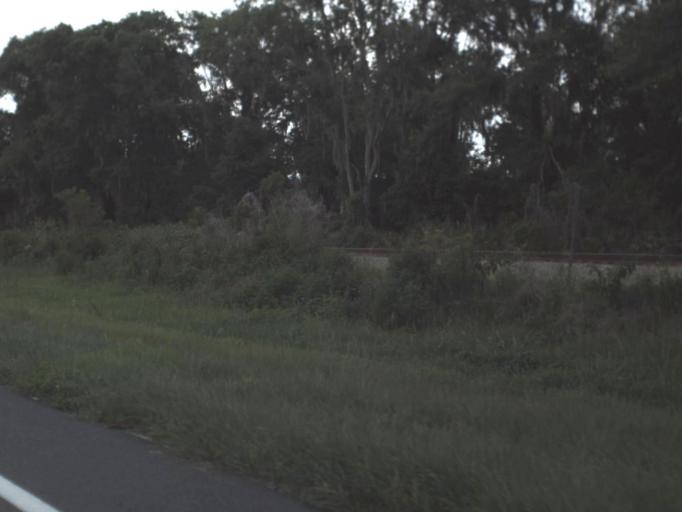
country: US
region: Florida
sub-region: Hamilton County
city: Jasper
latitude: 30.4081
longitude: -82.8432
